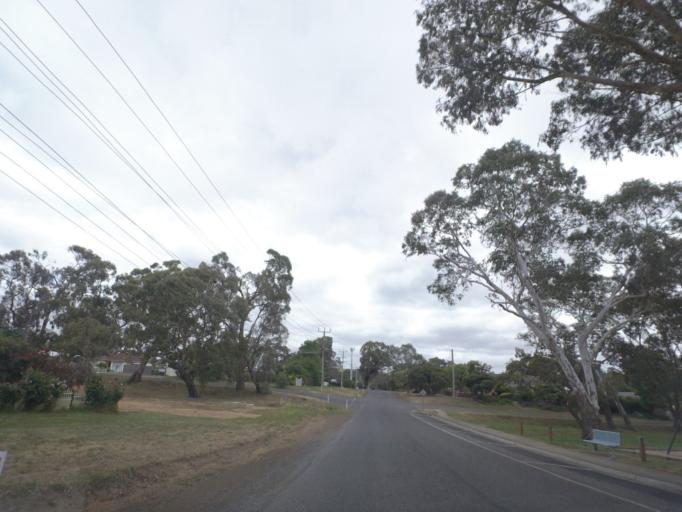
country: AU
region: Victoria
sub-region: Whittlesea
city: Whittlesea
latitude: -37.2029
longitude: 145.0431
